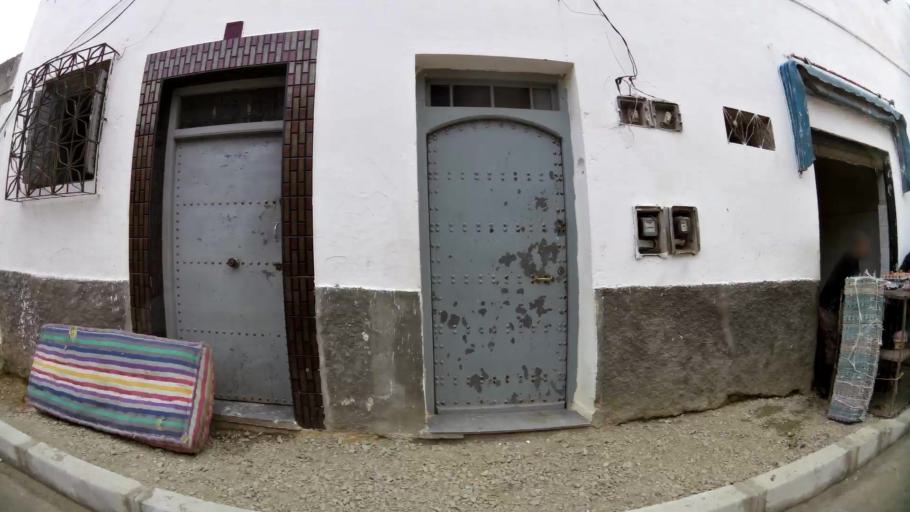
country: MA
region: Tanger-Tetouan
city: Tetouan
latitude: 35.5731
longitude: -5.3846
